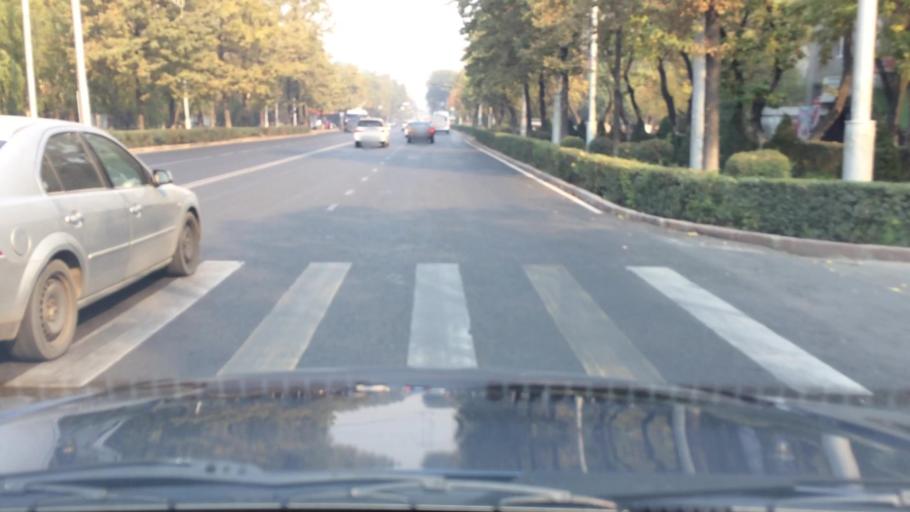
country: KG
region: Chuy
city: Bishkek
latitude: 42.8465
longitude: 74.5863
